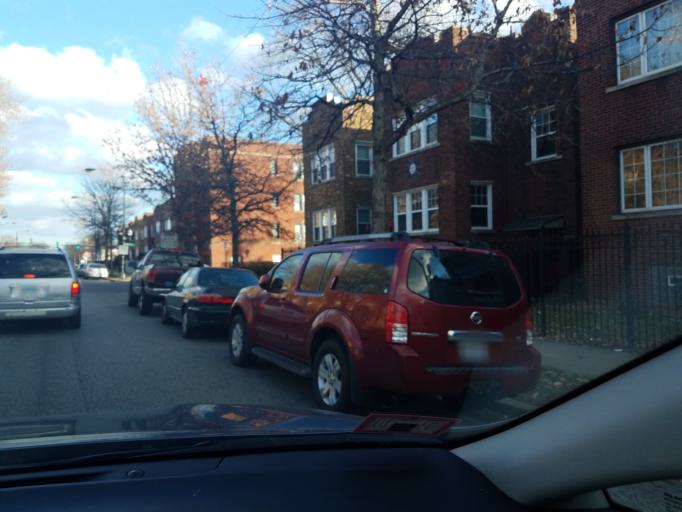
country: US
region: Illinois
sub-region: Cook County
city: Lincolnwood
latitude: 41.9466
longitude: -87.7046
